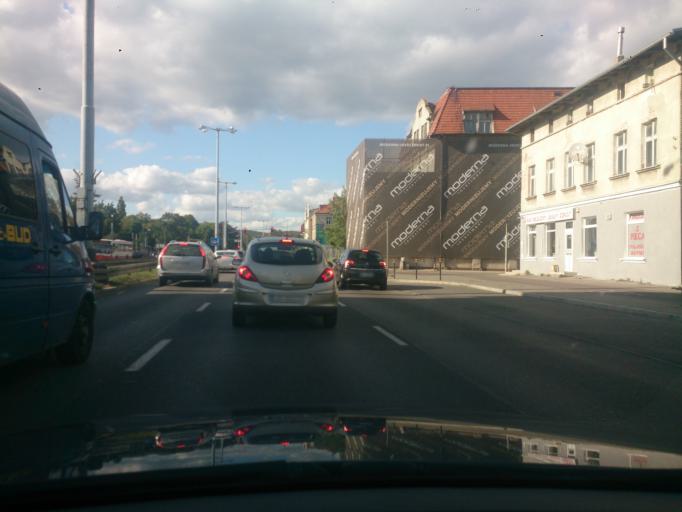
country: PL
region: Pomeranian Voivodeship
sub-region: Sopot
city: Sopot
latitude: 54.4089
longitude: 18.5686
